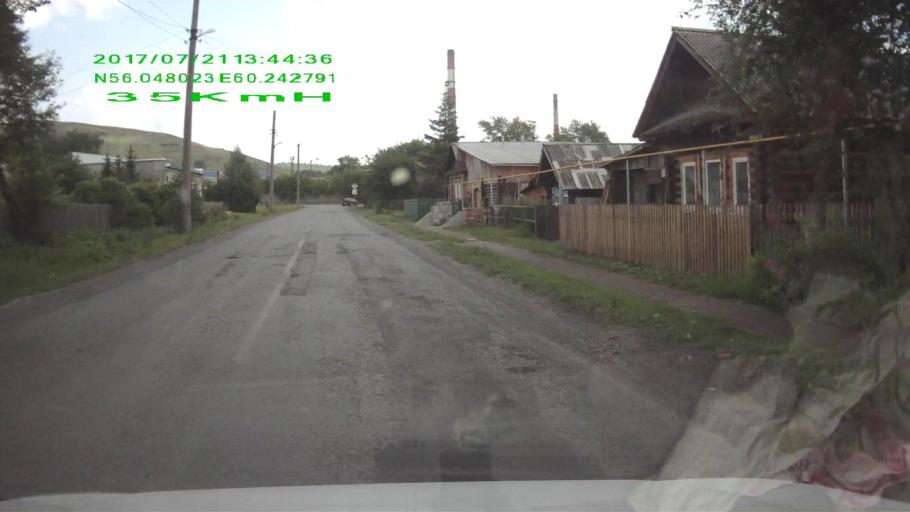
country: RU
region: Chelyabinsk
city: Verkhniy Ufaley
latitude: 56.0481
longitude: 60.2434
